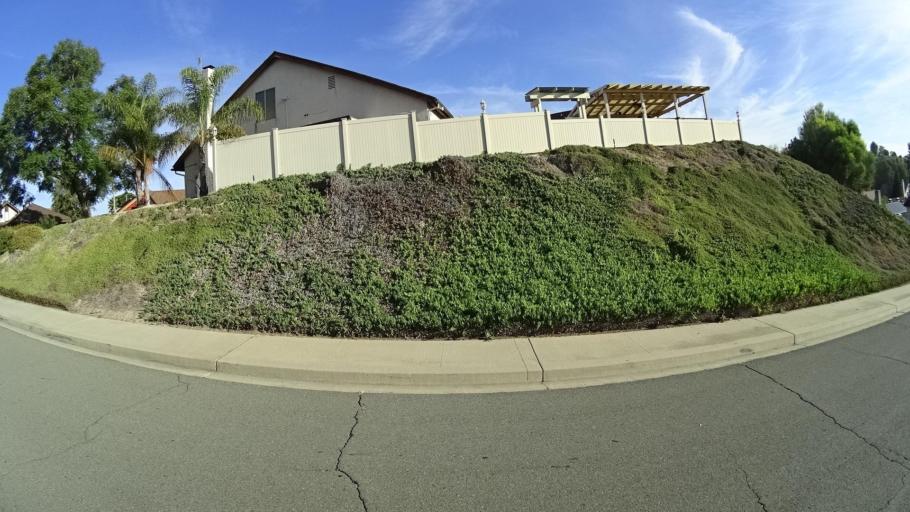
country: US
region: California
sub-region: San Diego County
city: Spring Valley
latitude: 32.7358
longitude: -116.9825
